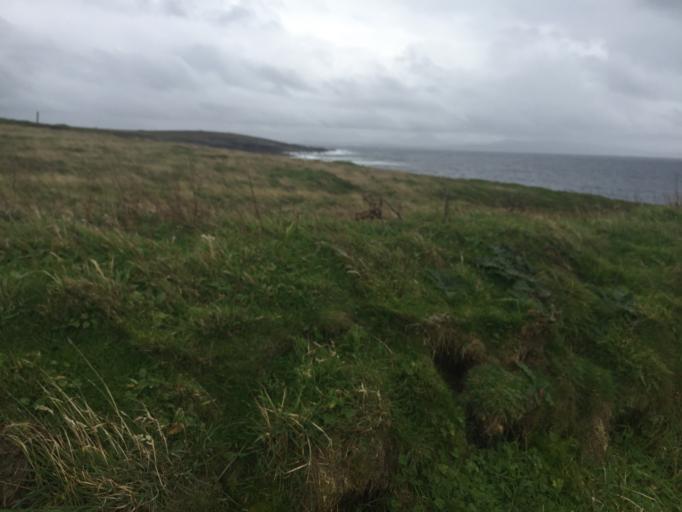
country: IE
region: Ulster
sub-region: County Donegal
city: Derrybeg
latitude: 55.2634
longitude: -8.2235
